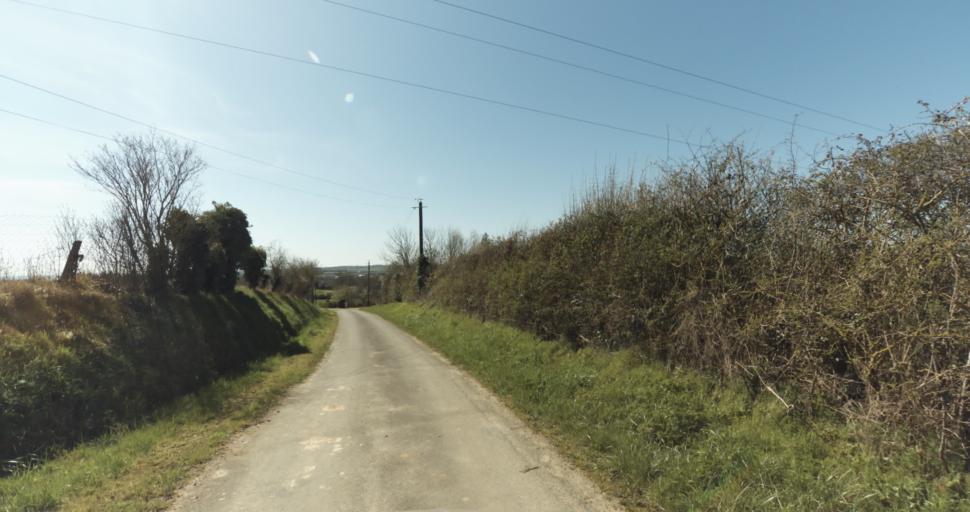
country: FR
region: Lower Normandy
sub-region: Departement du Calvados
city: Saint-Pierre-sur-Dives
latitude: 49.0586
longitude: -0.0160
